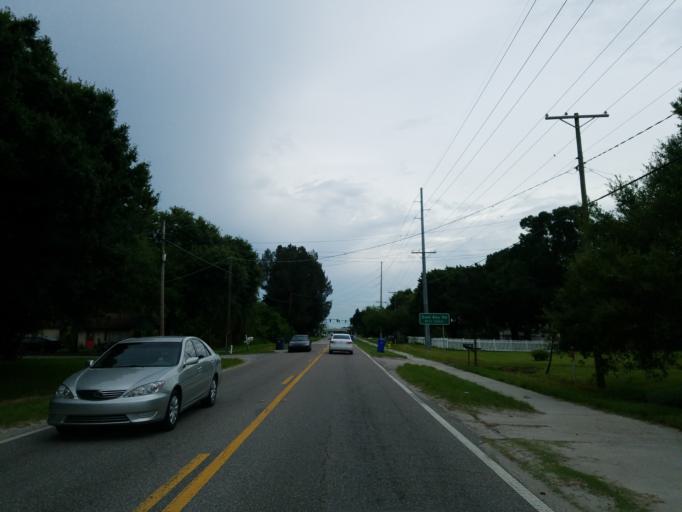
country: US
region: Florida
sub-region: Hillsborough County
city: Gibsonton
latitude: 27.8351
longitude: -82.3552
